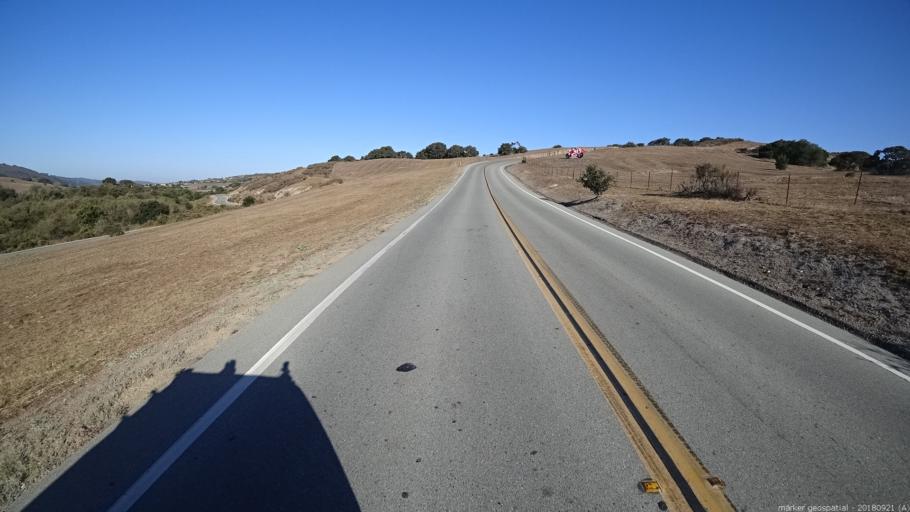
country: US
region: California
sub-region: Monterey County
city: Carmel Valley Village
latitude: 36.5713
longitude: -121.7617
